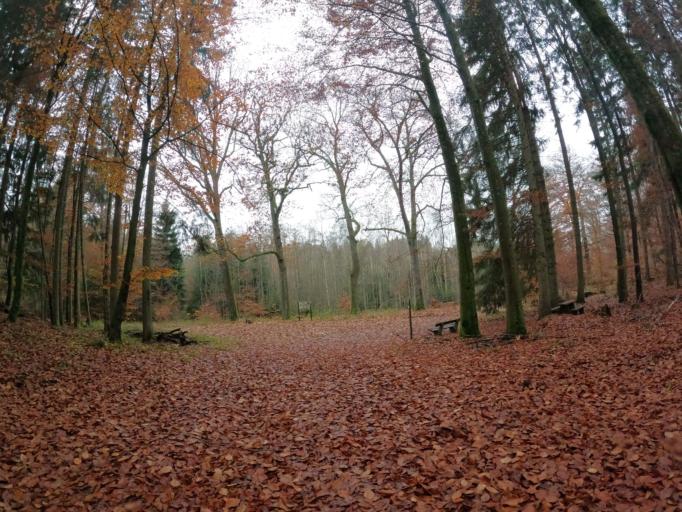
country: LU
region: Luxembourg
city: Heisdorf-sur-Alzette
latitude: 49.6689
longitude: 6.1651
